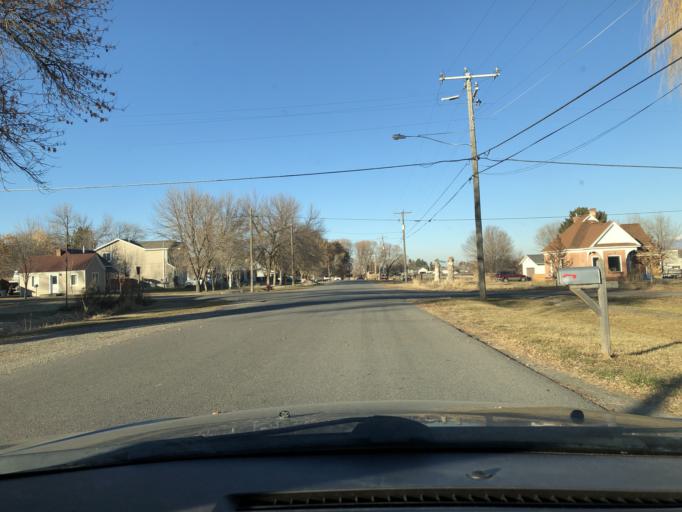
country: US
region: Utah
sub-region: Cache County
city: Wellsville
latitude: 41.6425
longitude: -111.9314
